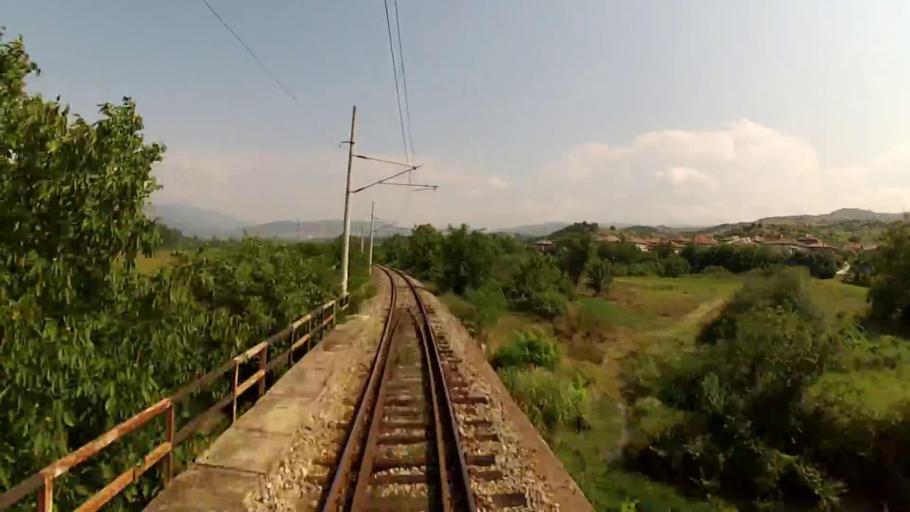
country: BG
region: Blagoevgrad
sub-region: Obshtina Strumyani
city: Strumyani
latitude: 41.6548
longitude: 23.1799
